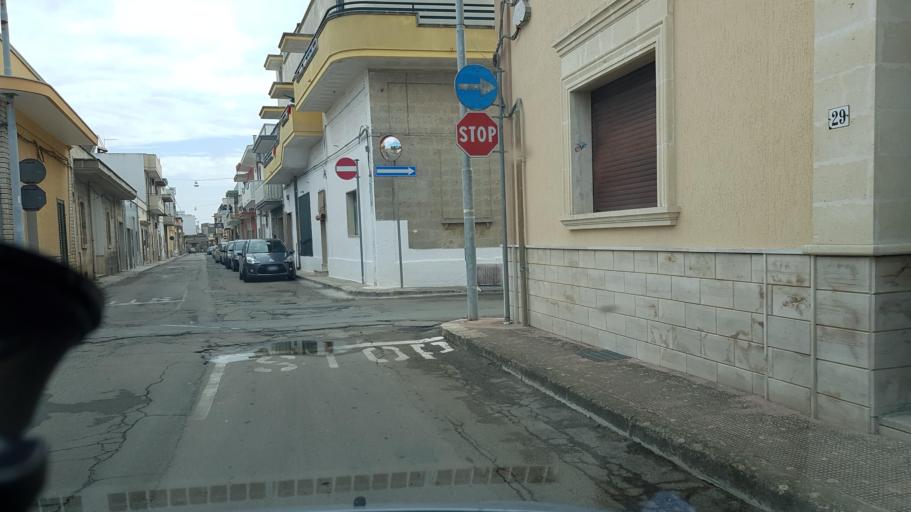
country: IT
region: Apulia
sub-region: Provincia di Brindisi
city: Torre Santa Susanna
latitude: 40.4713
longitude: 17.7407
